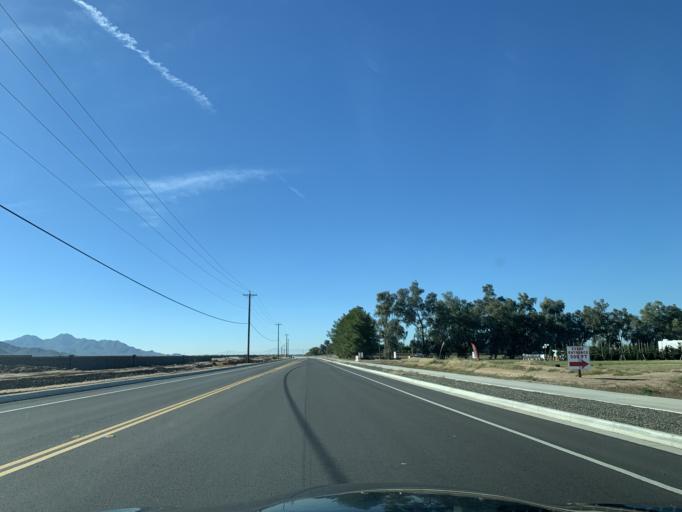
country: US
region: Arizona
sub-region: Maricopa County
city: Queen Creek
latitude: 33.2198
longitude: -111.5888
